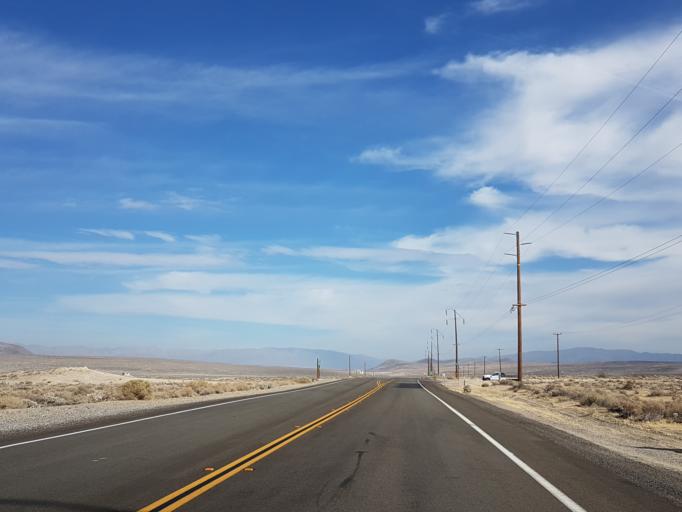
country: US
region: California
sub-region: Kern County
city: Ridgecrest
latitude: 35.6469
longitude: -117.5116
